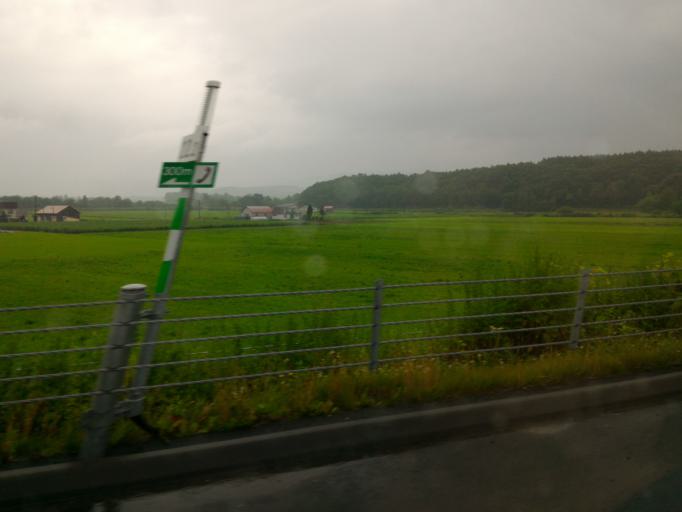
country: JP
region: Hokkaido
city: Nayoro
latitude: 44.4938
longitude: 142.3509
